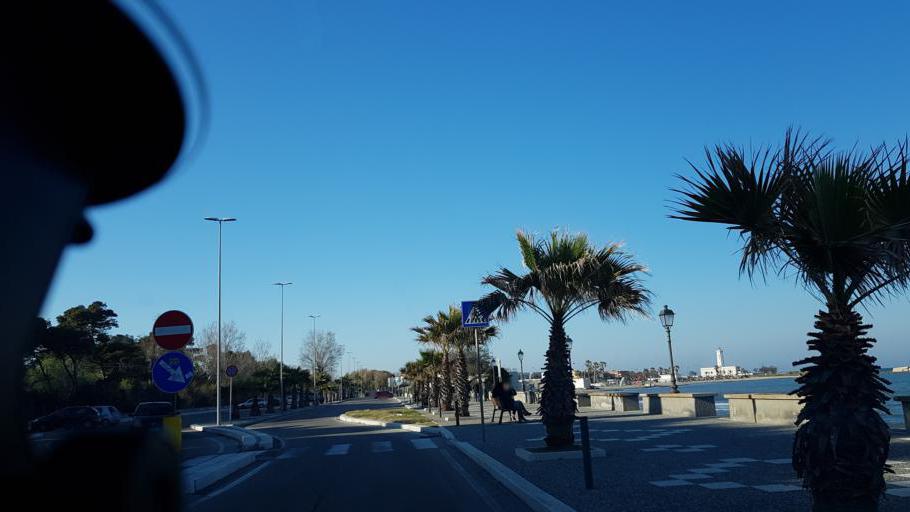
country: IT
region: Apulia
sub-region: Provincia di Lecce
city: Struda
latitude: 40.3852
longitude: 18.3046
